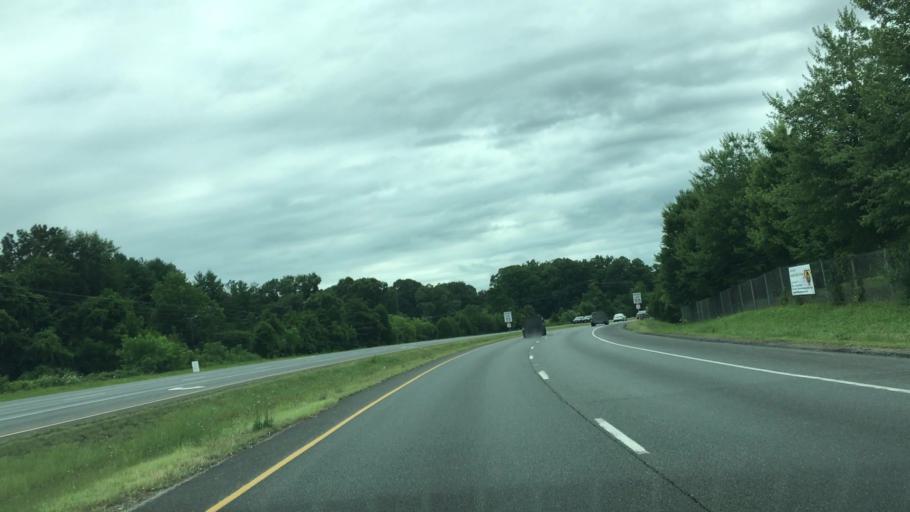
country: US
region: Virginia
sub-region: Prince William County
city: Buckhall
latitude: 38.7344
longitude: -77.4329
